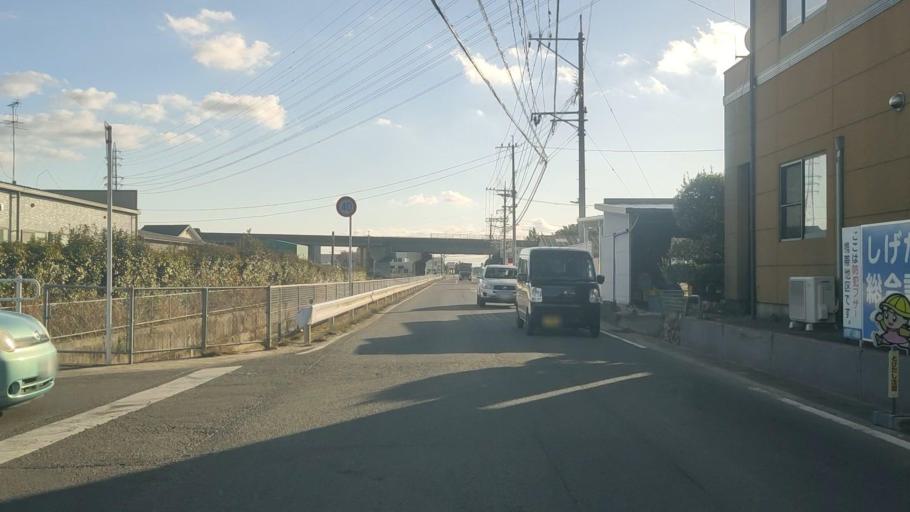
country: JP
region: Saga Prefecture
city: Saga-shi
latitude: 33.3199
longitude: 130.2674
